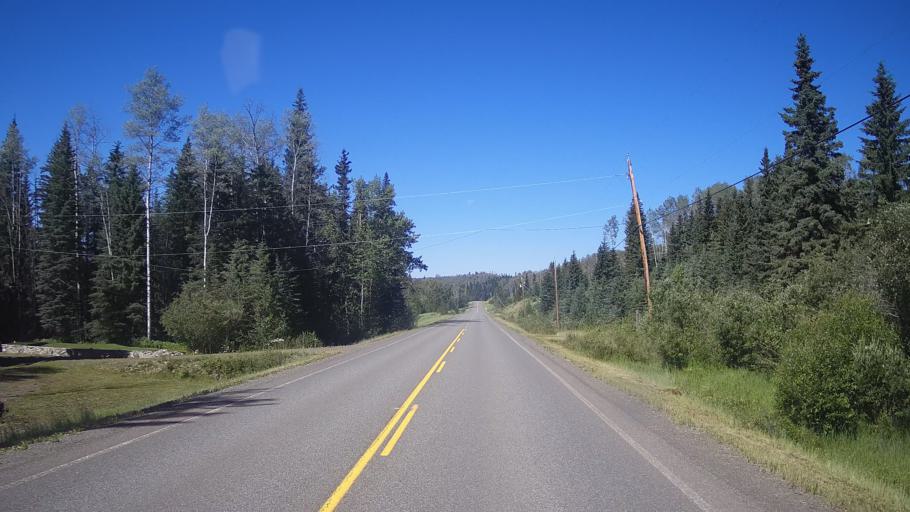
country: CA
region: British Columbia
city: Kamloops
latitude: 51.5051
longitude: -120.6106
